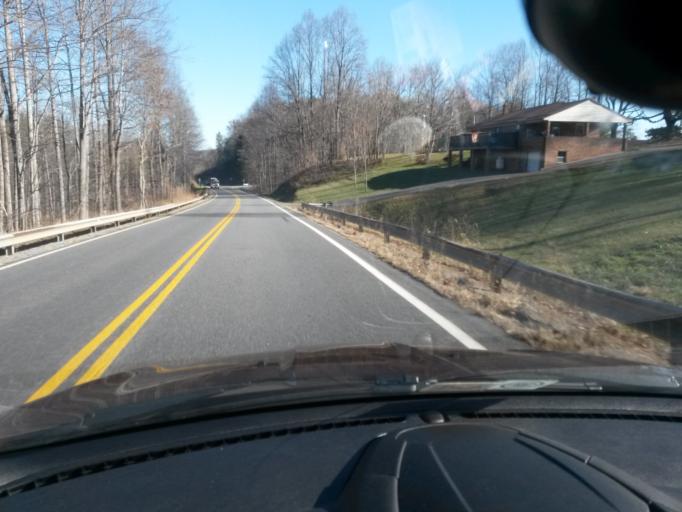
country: US
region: Virginia
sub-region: Patrick County
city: Patrick Springs
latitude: 36.7382
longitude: -80.2119
